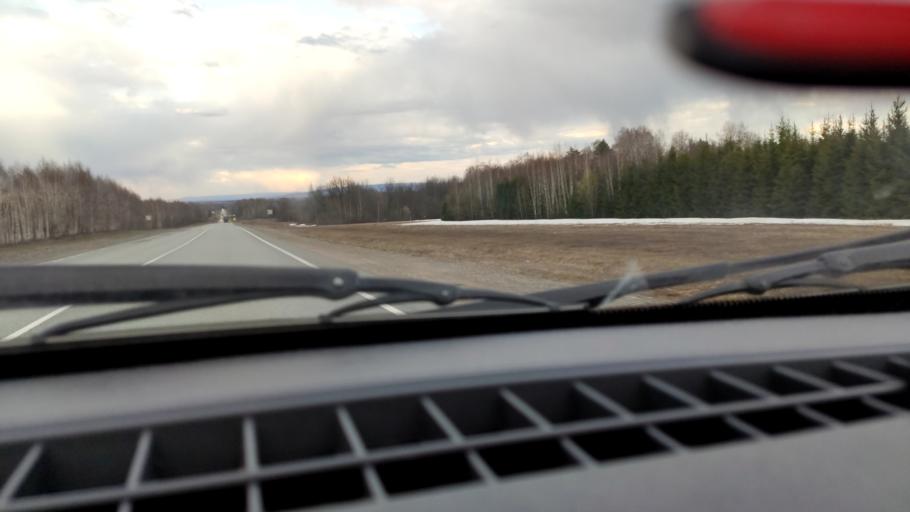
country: RU
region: Bashkortostan
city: Kudeyevskiy
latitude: 54.8109
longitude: 56.6558
